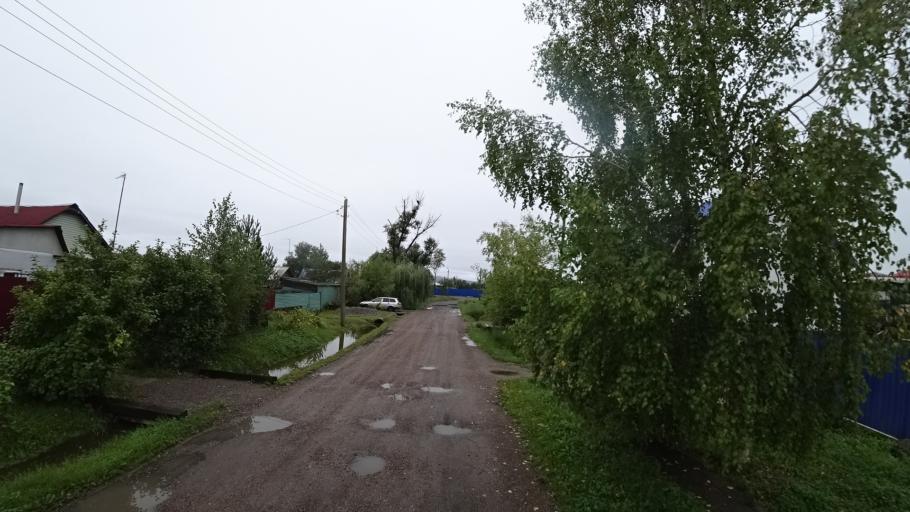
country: RU
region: Primorskiy
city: Monastyrishche
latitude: 44.2054
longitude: 132.4519
